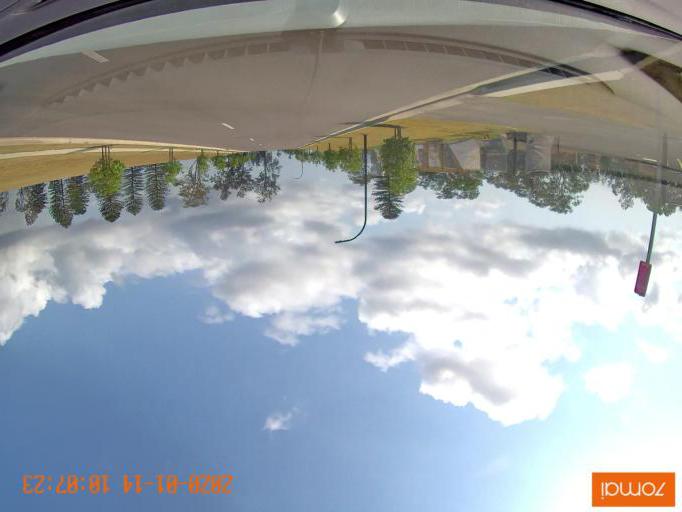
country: AU
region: New South Wales
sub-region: Wyong Shire
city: Kingfisher Shores
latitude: -33.1247
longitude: 151.5407
